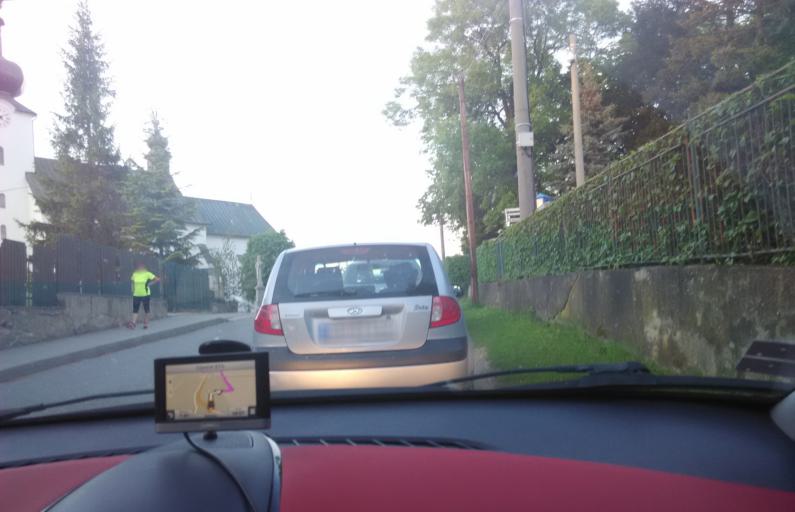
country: SK
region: Presovsky
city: Sabinov
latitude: 49.0809
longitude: 21.0831
